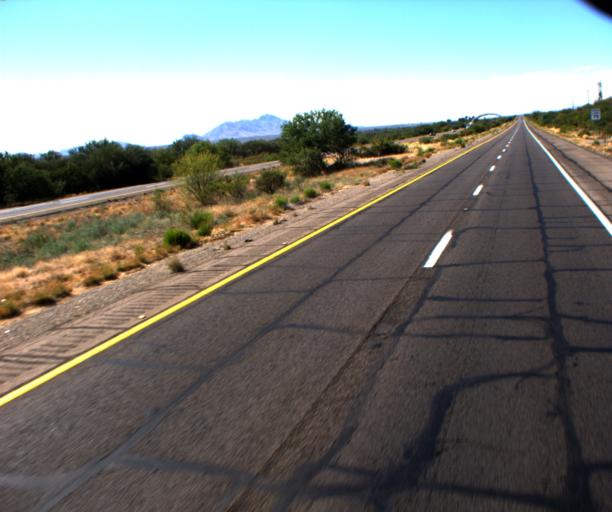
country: US
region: Arizona
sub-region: Santa Cruz County
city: Tubac
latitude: 31.6681
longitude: -111.0629
